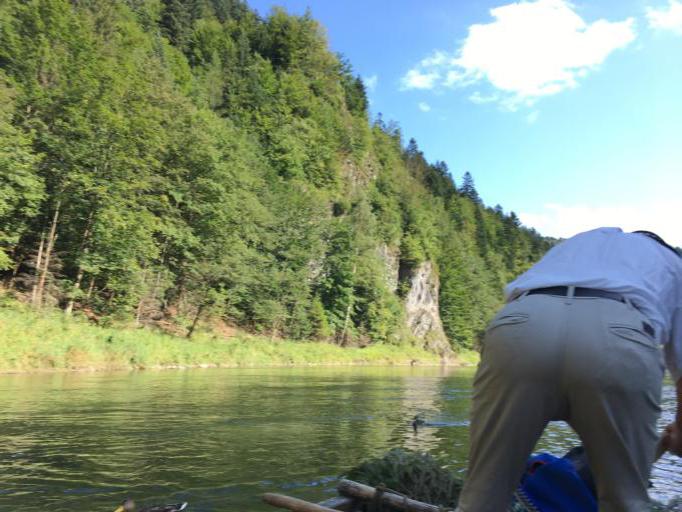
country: PL
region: Lesser Poland Voivodeship
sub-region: Powiat nowotarski
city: Kroscienko nad Dunajcem
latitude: 49.4024
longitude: 20.4275
